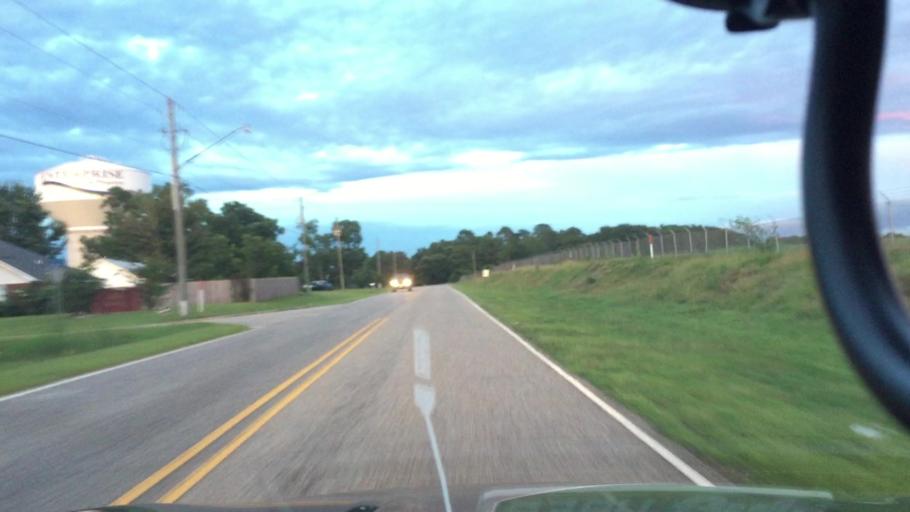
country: US
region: Alabama
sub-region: Coffee County
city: Enterprise
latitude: 31.3676
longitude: -85.8496
